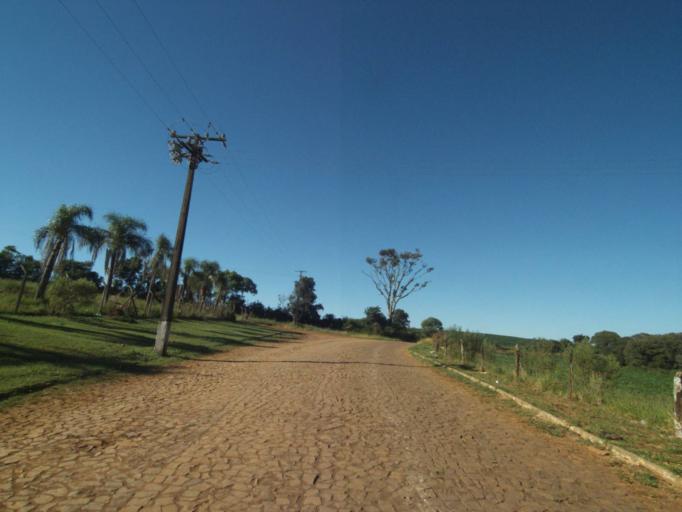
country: BR
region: Parana
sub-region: Pinhao
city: Pinhao
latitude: -25.8452
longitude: -52.0317
